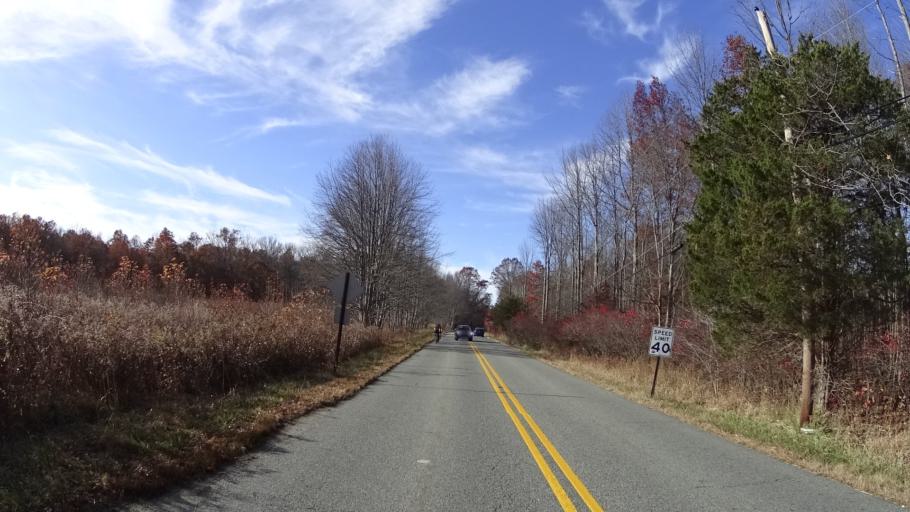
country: US
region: New Jersey
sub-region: Union County
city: Berkeley Heights
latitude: 40.7086
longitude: -74.4779
